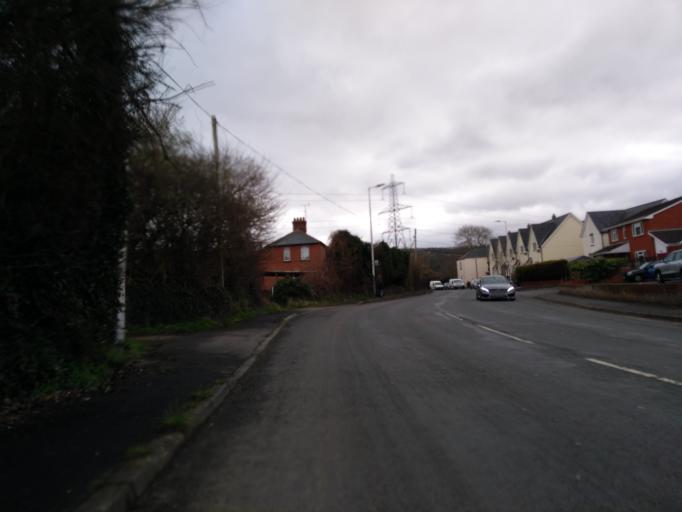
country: GB
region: England
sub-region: Devon
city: Exeter
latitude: 50.7697
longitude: -3.5075
